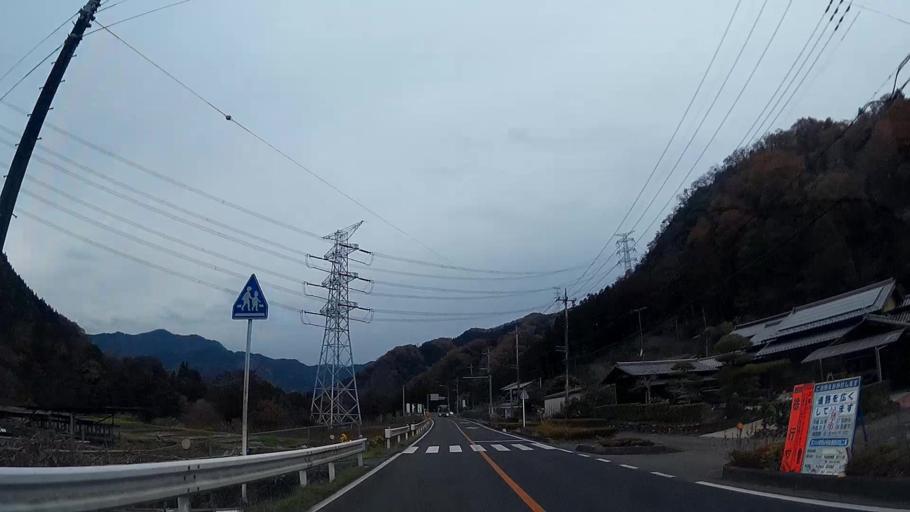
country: JP
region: Saitama
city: Chichibu
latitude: 35.9589
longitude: 139.0051
